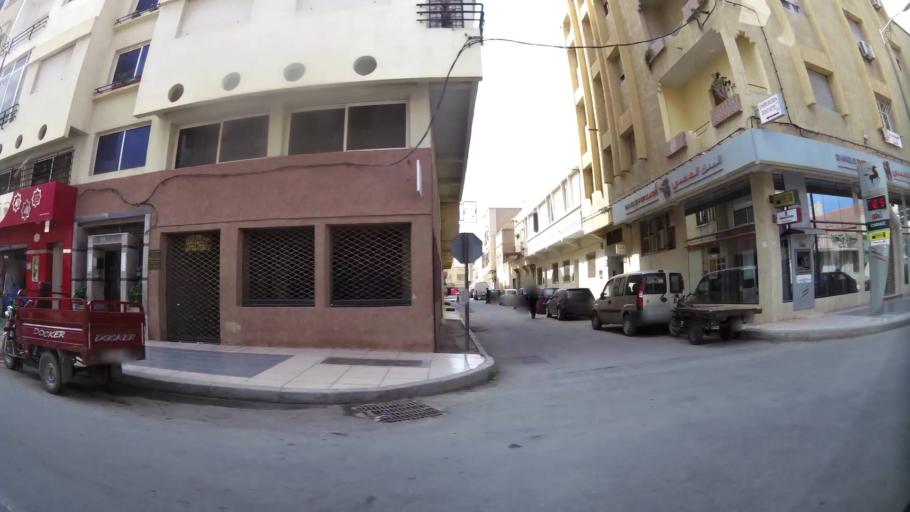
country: MA
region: Oriental
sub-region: Oujda-Angad
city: Oujda
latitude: 34.6846
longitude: -1.9118
